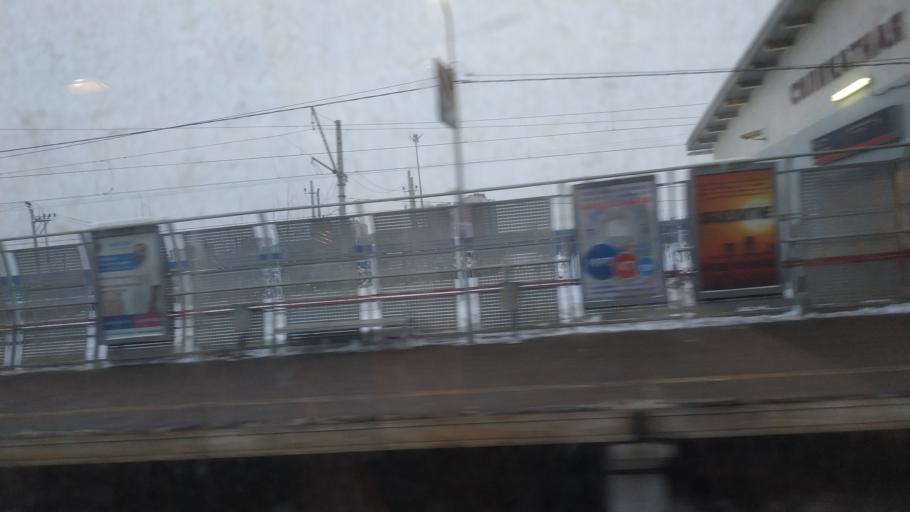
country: RU
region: Moskovskaya
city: Shcherbinka
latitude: 55.4706
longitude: 37.5555
